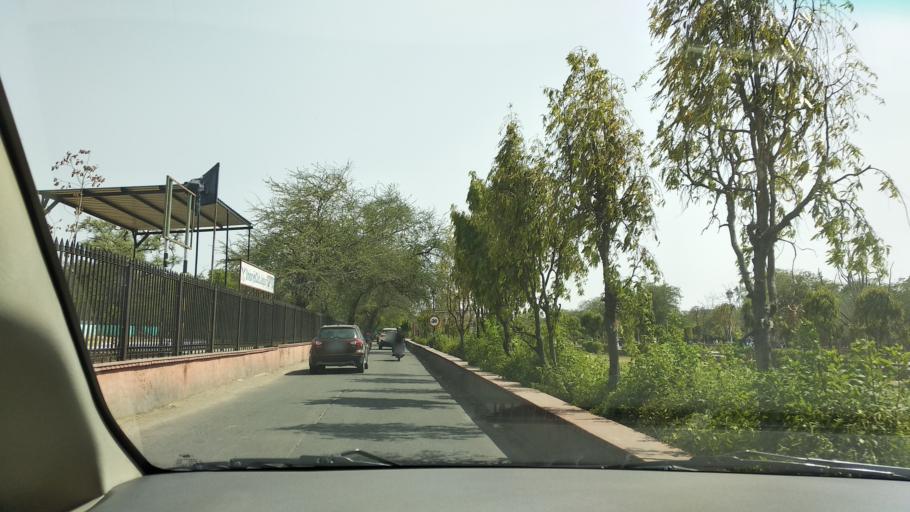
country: IN
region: Rajasthan
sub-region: Jaipur
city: Jaipur
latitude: 26.9149
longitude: 75.8206
